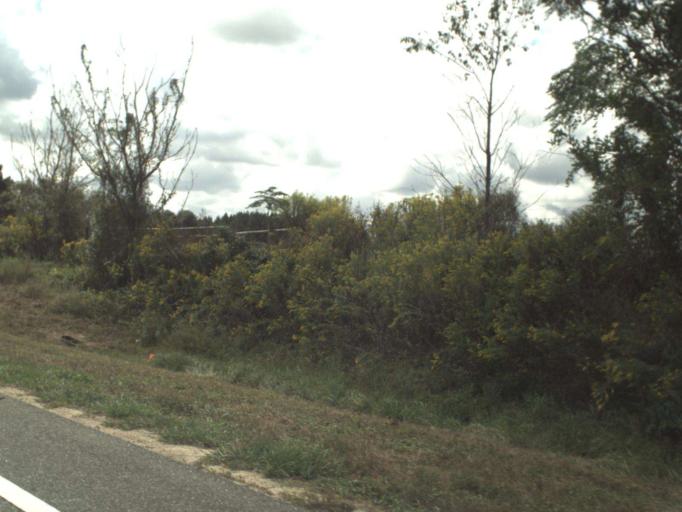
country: US
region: Florida
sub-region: Washington County
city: Chipley
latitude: 30.8261
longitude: -85.5045
